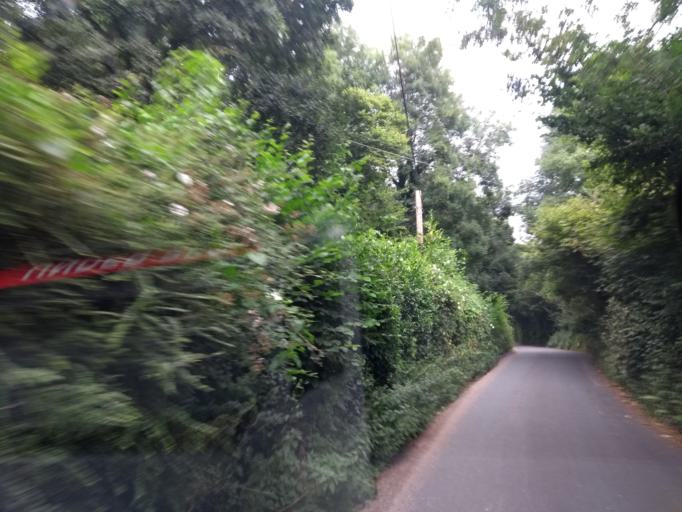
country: GB
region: England
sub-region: Somerset
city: Chard
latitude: 50.8703
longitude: -3.0785
